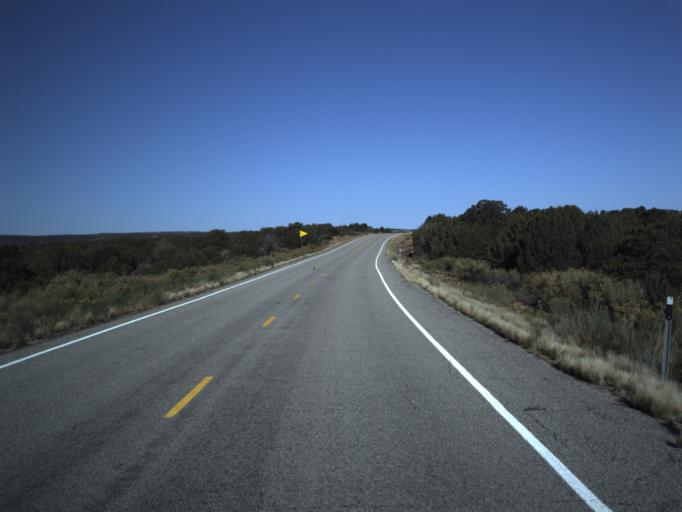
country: US
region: Utah
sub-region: San Juan County
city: Blanding
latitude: 37.5446
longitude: -109.9821
